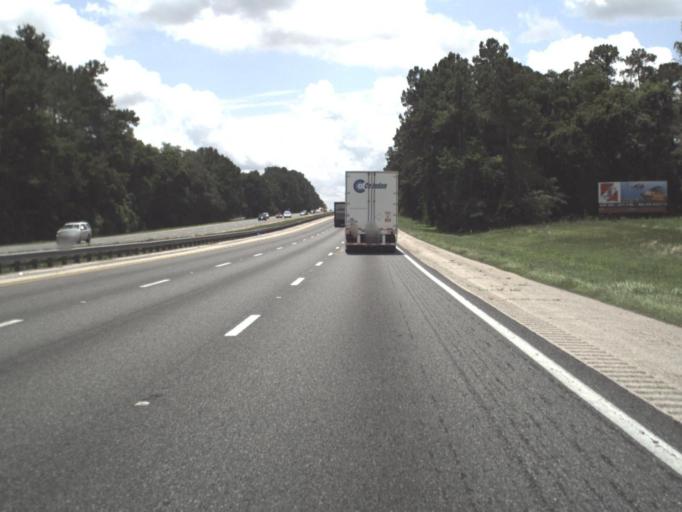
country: US
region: Florida
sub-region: Alachua County
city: High Springs
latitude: 29.8249
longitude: -82.5203
